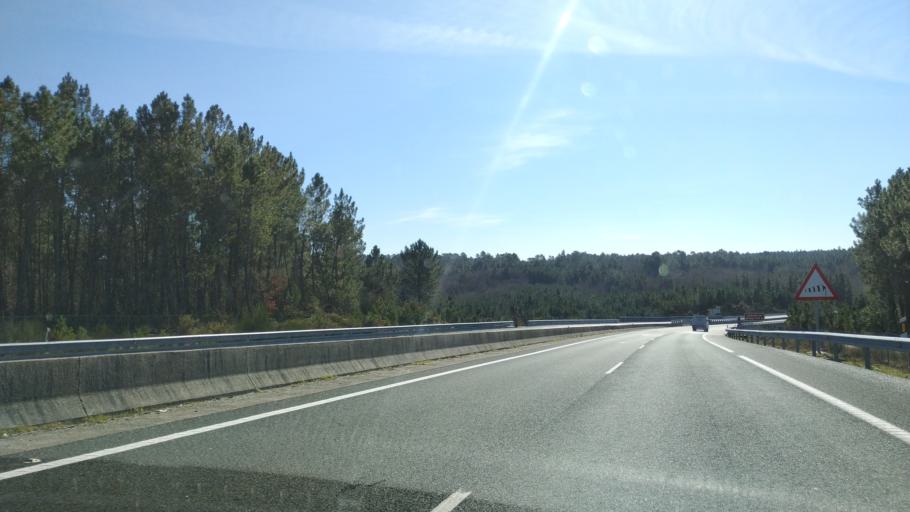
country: ES
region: Galicia
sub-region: Provincia de Ourense
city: Pinor
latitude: 42.4862
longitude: -8.0221
